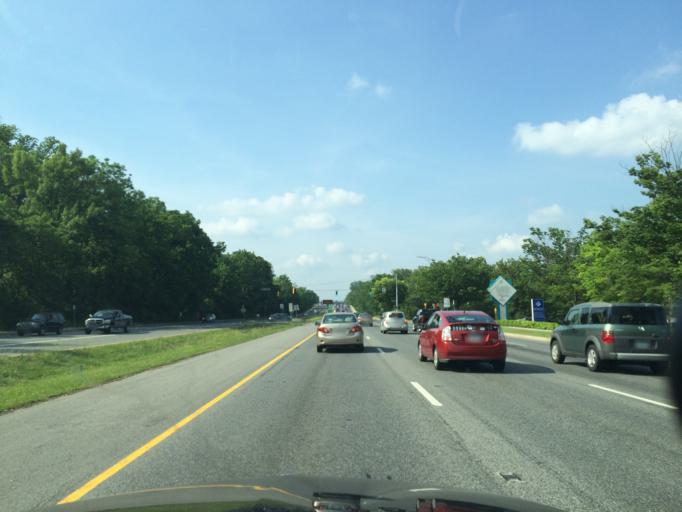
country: US
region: Maryland
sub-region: Montgomery County
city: Rossmoor
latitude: 39.1027
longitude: -77.0767
